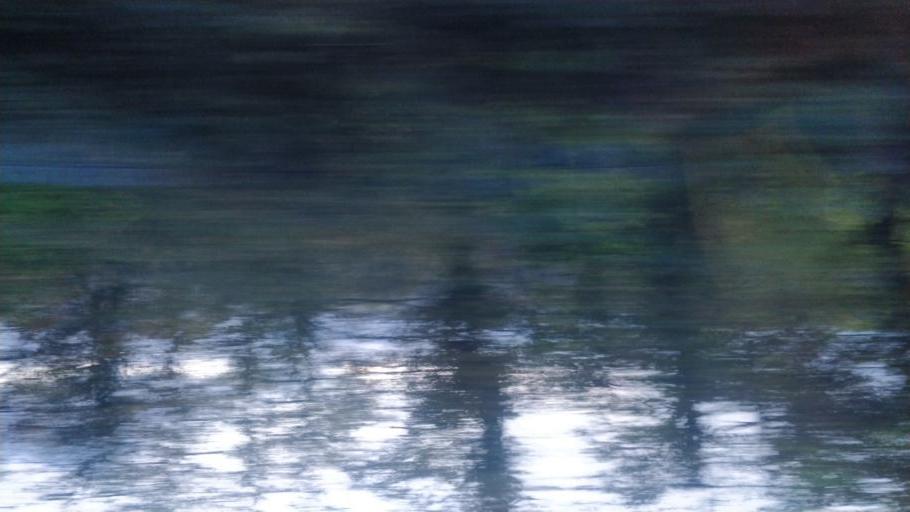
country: GB
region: England
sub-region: Lancashire
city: Appley Bridge
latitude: 53.5685
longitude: -2.7112
